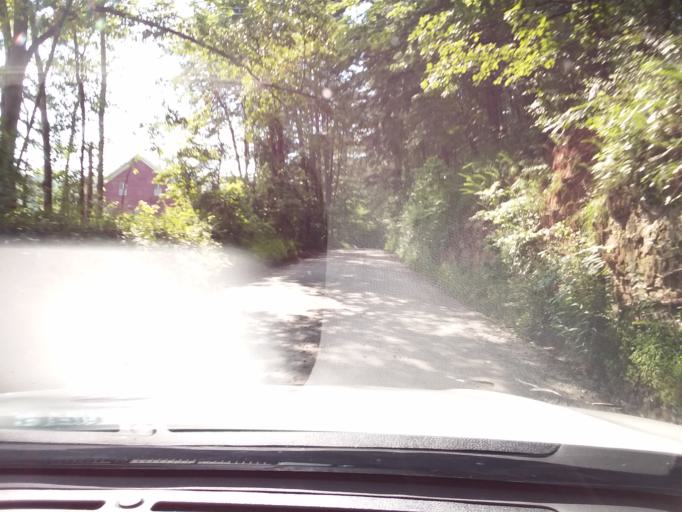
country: US
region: Georgia
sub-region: Habersham County
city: Clarkesville
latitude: 34.7205
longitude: -83.4476
